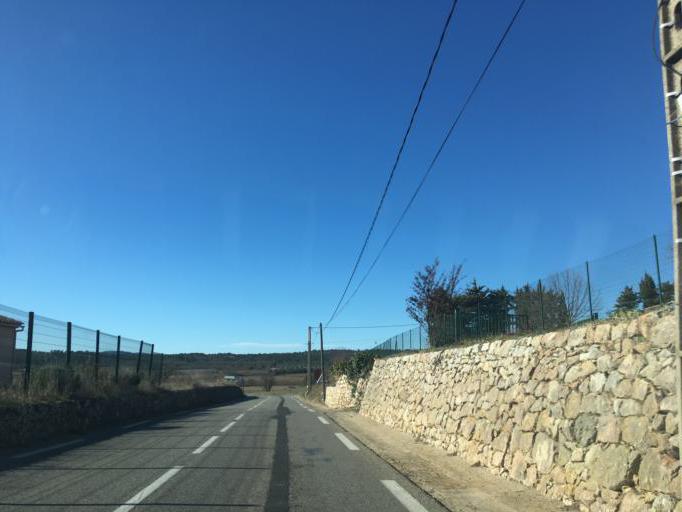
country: FR
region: Provence-Alpes-Cote d'Azur
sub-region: Departement du Var
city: Barjols
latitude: 43.5935
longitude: 6.0127
